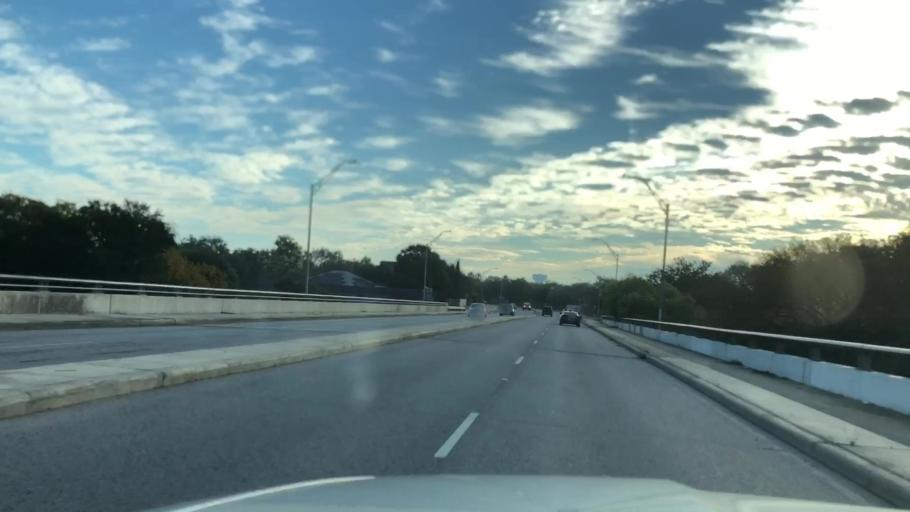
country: US
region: Texas
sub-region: Bexar County
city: Leon Valley
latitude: 29.5415
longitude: -98.6323
